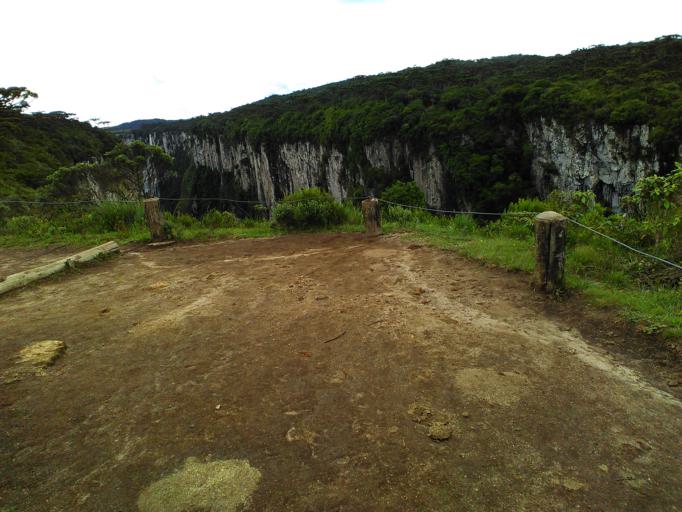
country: BR
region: Rio Grande do Sul
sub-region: Torres
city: Torres
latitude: -29.1604
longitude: -50.0793
